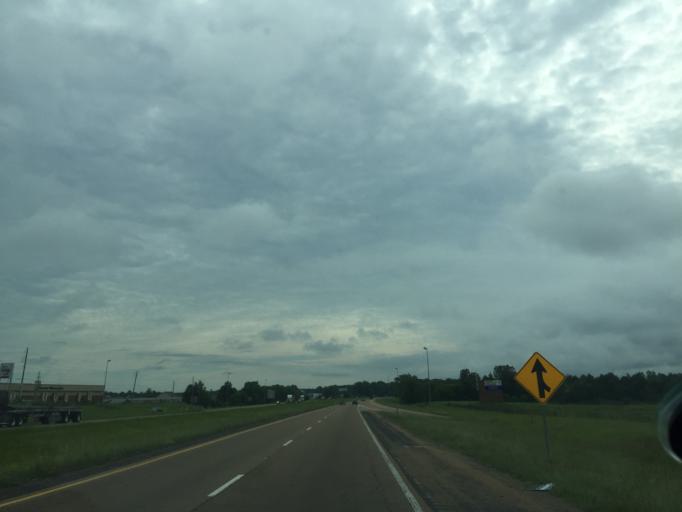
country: US
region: Mississippi
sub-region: Rankin County
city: Brandon
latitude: 32.2784
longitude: -90.0329
